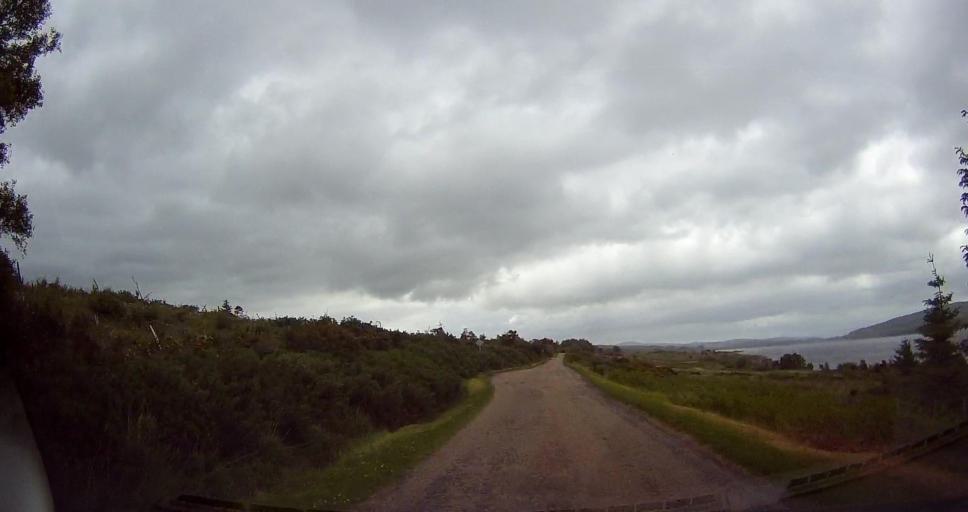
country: GB
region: Scotland
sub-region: Highland
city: Evanton
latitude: 58.0681
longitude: -4.4541
